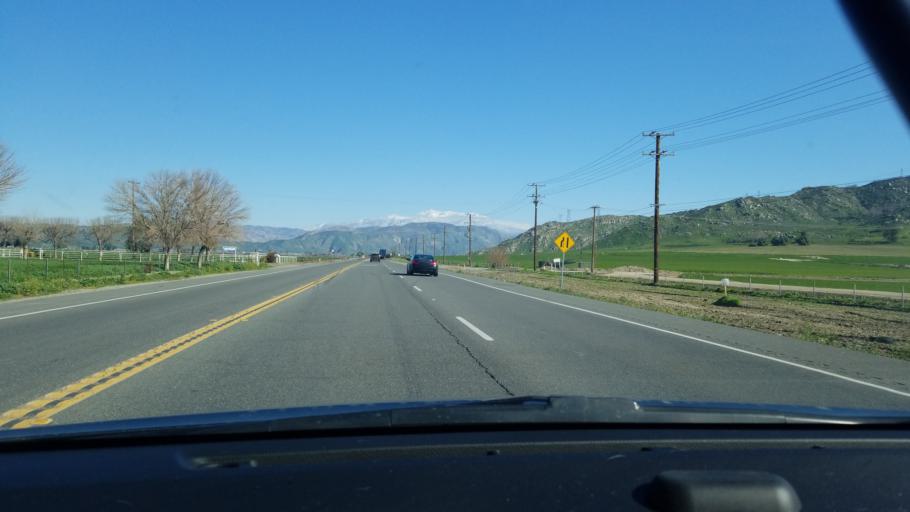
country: US
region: California
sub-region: Riverside County
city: Lakeview
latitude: 33.8399
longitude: -117.0894
